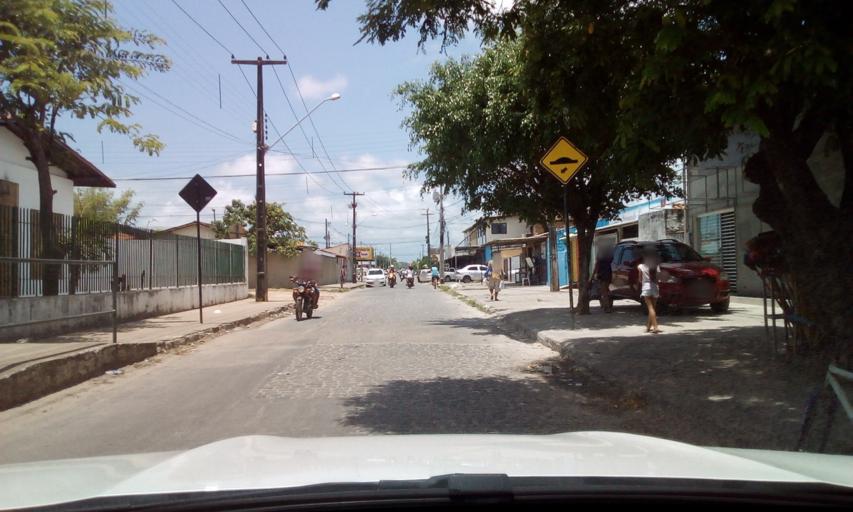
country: BR
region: Paraiba
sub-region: Joao Pessoa
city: Joao Pessoa
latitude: -7.1702
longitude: -34.8367
